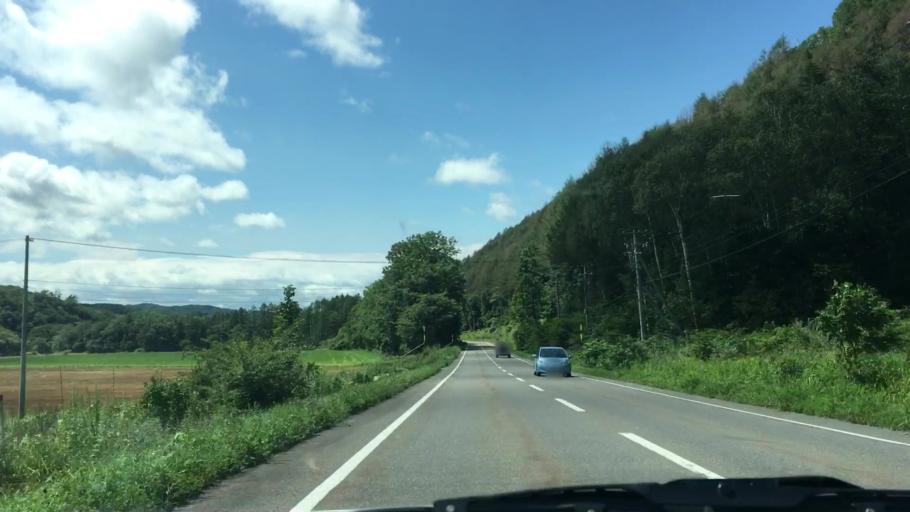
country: JP
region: Hokkaido
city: Otofuke
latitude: 43.2928
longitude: 143.6649
